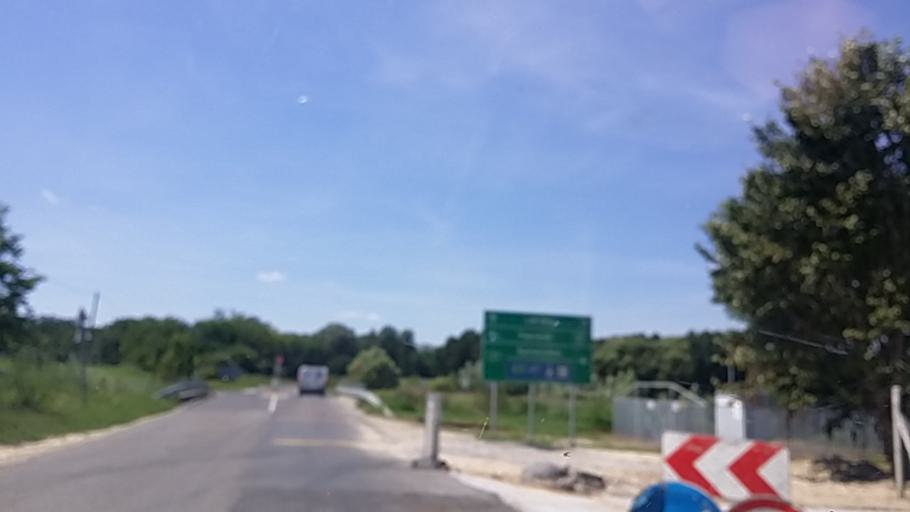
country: HU
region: Somogy
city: Karad
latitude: 46.7265
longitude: 17.7772
